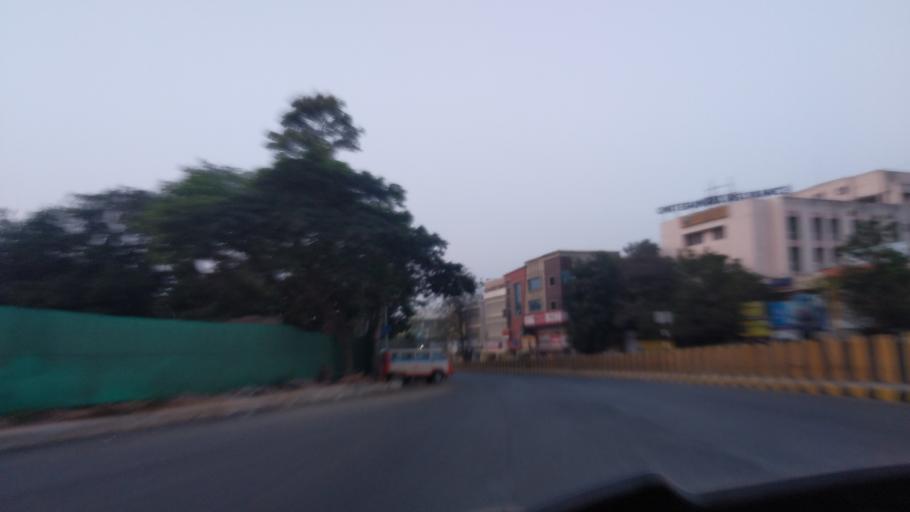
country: IN
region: Tamil Nadu
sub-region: Coimbatore
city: Coimbatore
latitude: 11.0078
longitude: 76.9670
